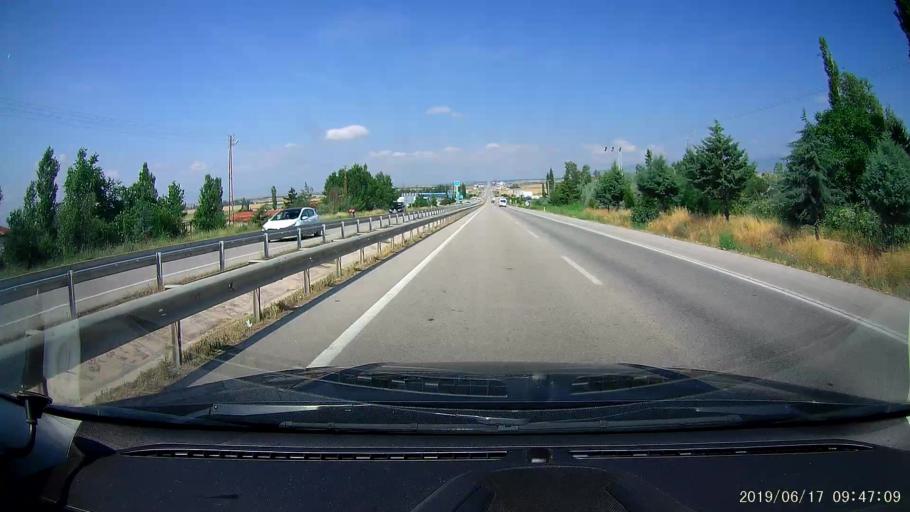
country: TR
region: Amasya
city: Suluova
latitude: 40.8772
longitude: 35.5855
